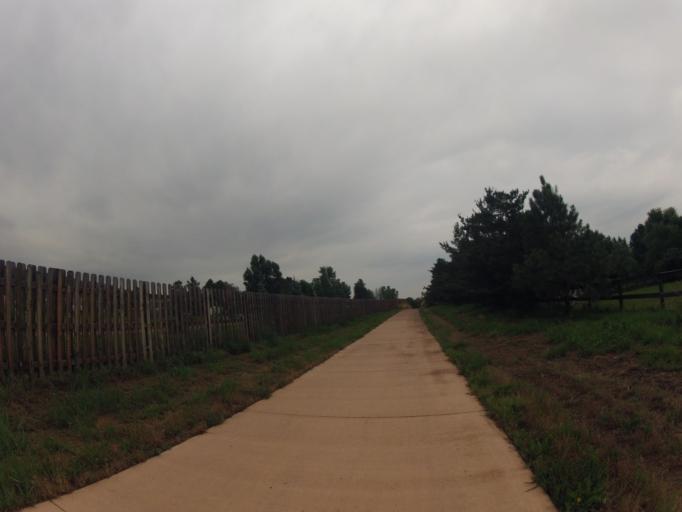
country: US
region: Colorado
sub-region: Larimer County
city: Fort Collins
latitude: 40.5318
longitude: -105.1271
